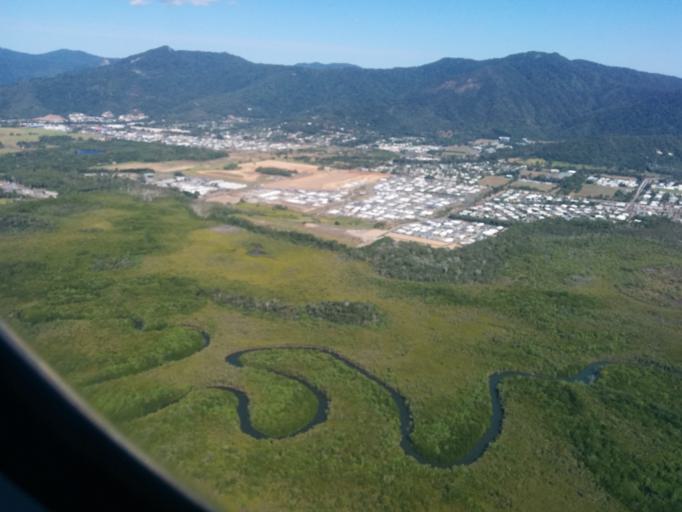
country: AU
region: Queensland
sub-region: Cairns
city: Yorkeys Knob
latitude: -16.8133
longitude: 145.7197
